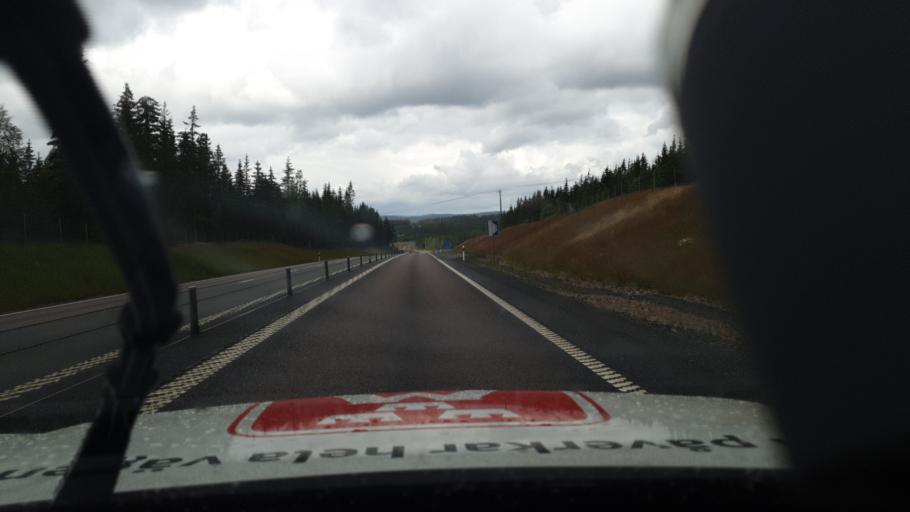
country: SE
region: Joenkoeping
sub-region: Mullsjo Kommun
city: Mullsjoe
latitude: 57.8817
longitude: 13.9112
